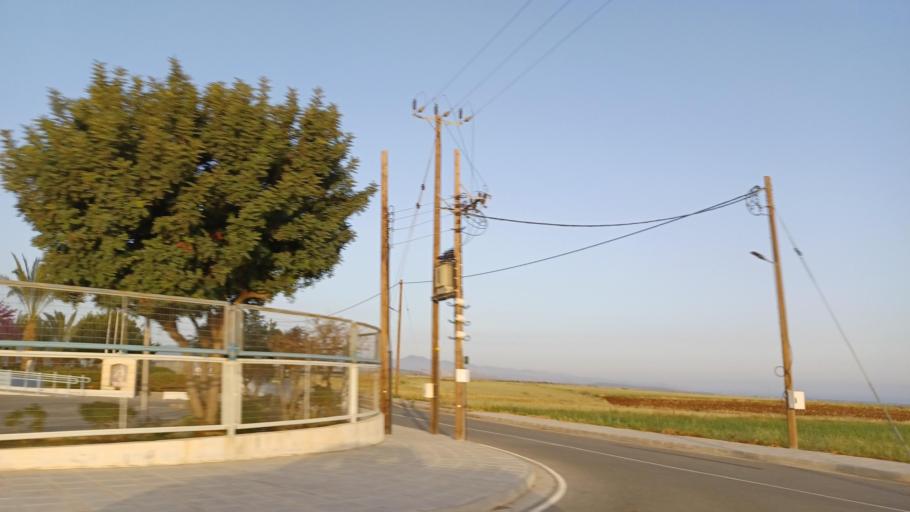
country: CY
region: Lefkosia
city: Astromeritis
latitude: 35.0944
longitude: 33.0152
